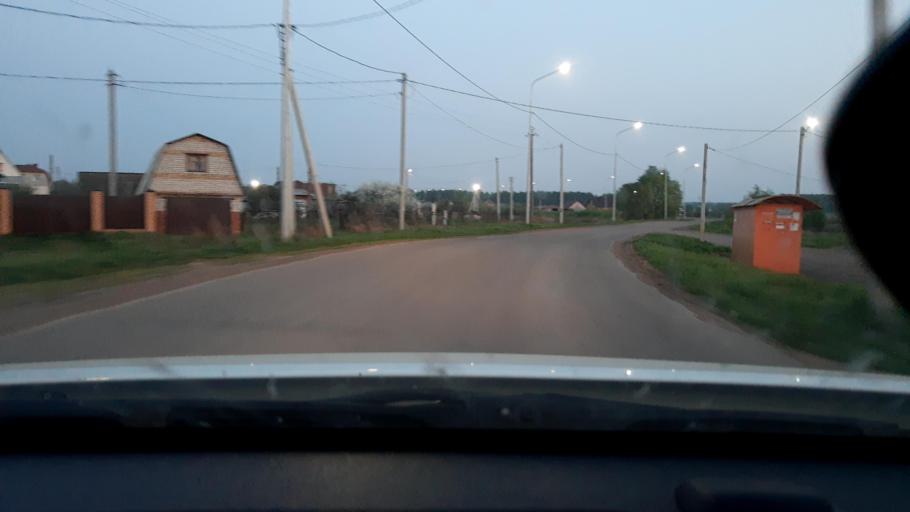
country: RU
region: Bashkortostan
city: Avdon
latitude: 54.5463
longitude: 55.7607
